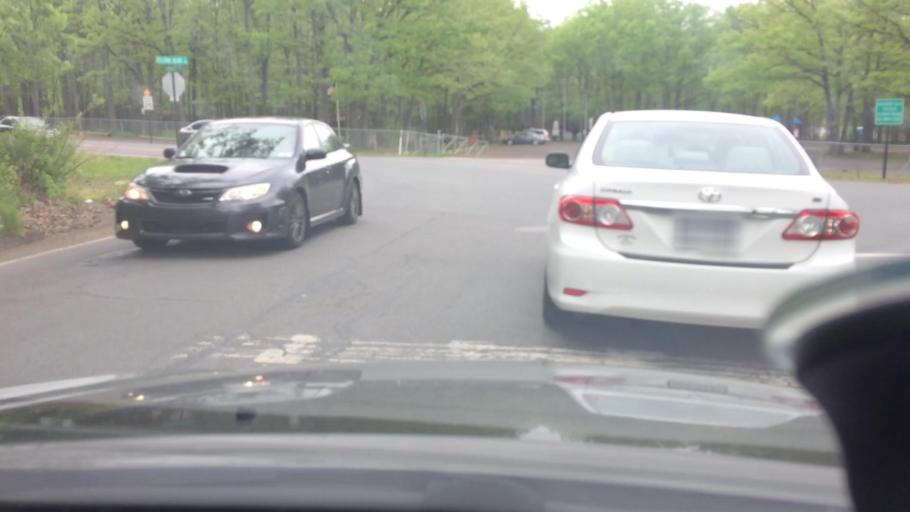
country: US
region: Pennsylvania
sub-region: Luzerne County
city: West Hazleton
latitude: 40.9801
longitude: -76.0077
